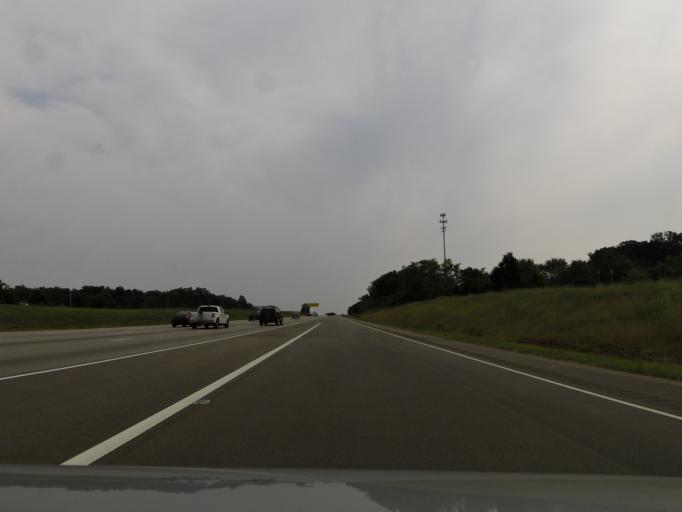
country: US
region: Ohio
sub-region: Warren County
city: Springboro
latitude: 39.5664
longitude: -84.2647
